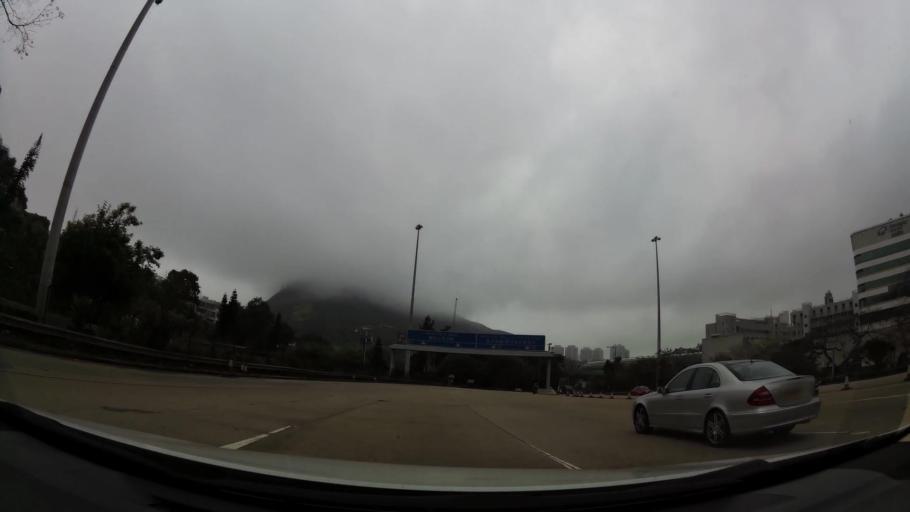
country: HK
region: Wanchai
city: Wan Chai
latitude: 22.2510
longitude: 114.1780
